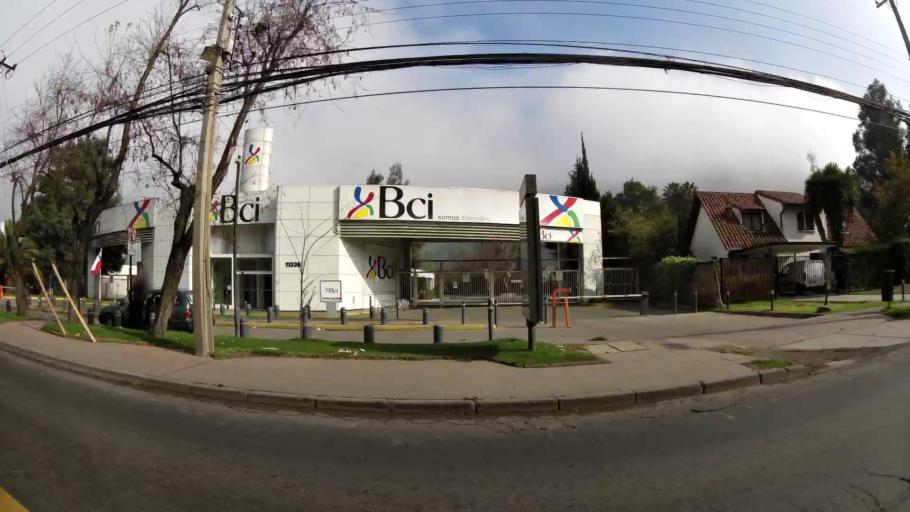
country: CL
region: Santiago Metropolitan
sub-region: Provincia de Santiago
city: Villa Presidente Frei, Nunoa, Santiago, Chile
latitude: -33.3777
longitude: -70.5281
